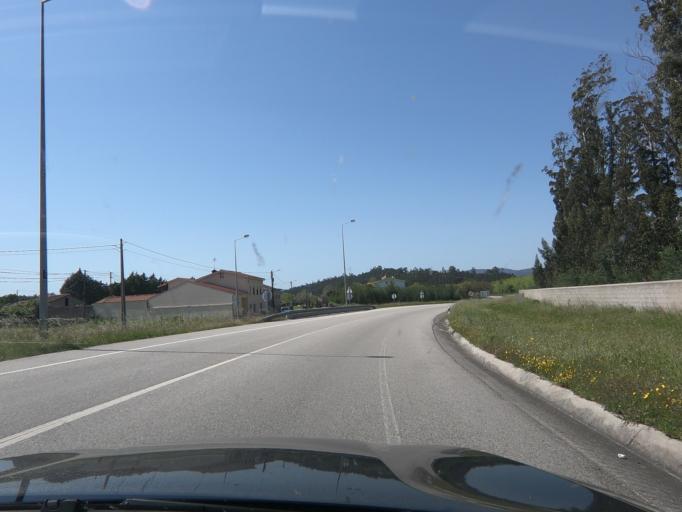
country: PT
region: Coimbra
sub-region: Lousa
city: Lousa
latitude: 40.1367
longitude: -8.2511
